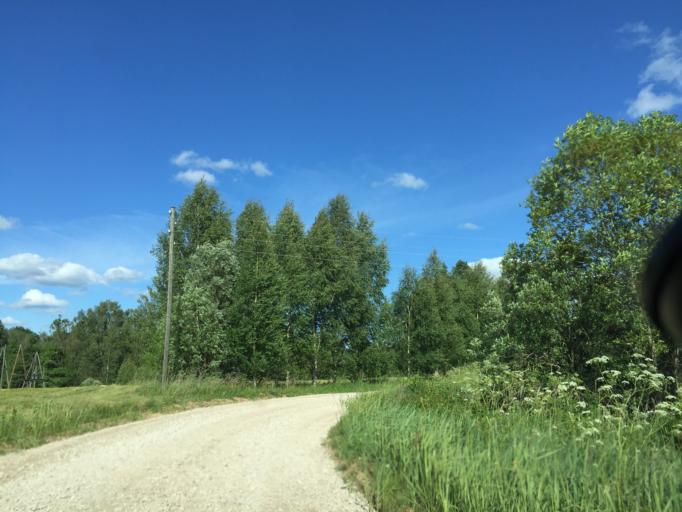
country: LV
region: Vecumnieki
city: Vecumnieki
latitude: 56.4214
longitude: 24.6112
